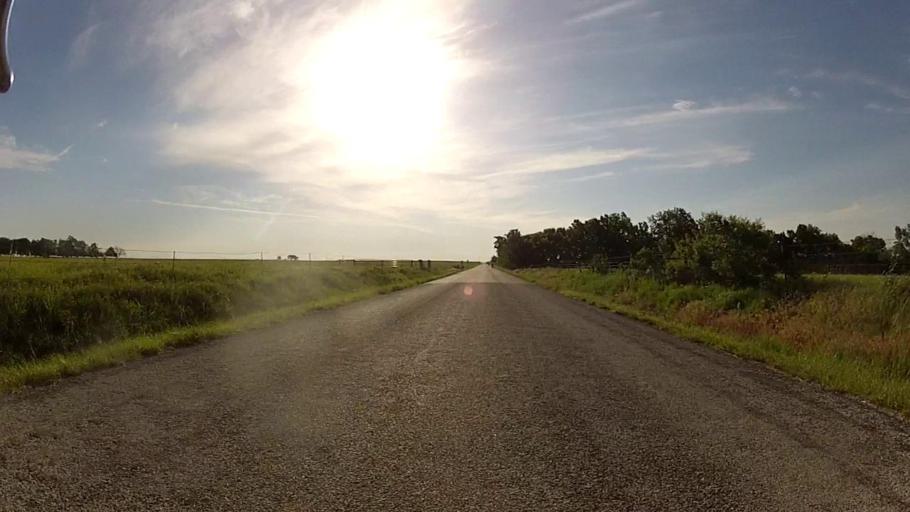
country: US
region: Kansas
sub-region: Cowley County
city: Arkansas City
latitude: 37.0485
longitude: -96.8374
